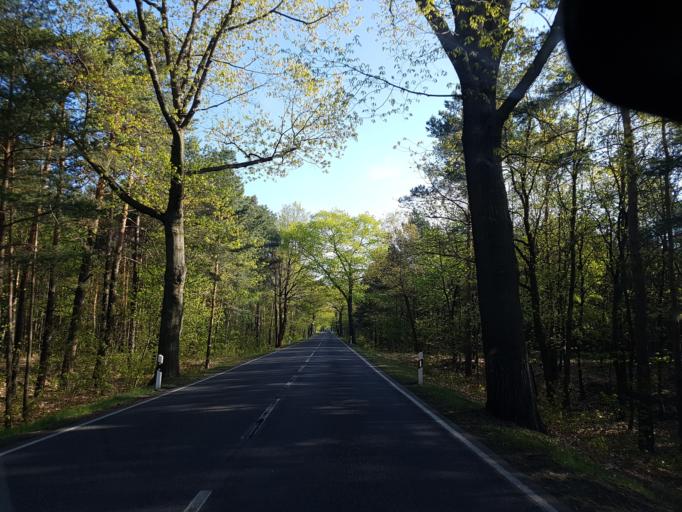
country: DE
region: Brandenburg
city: Grossraschen
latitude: 51.6136
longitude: 14.0219
